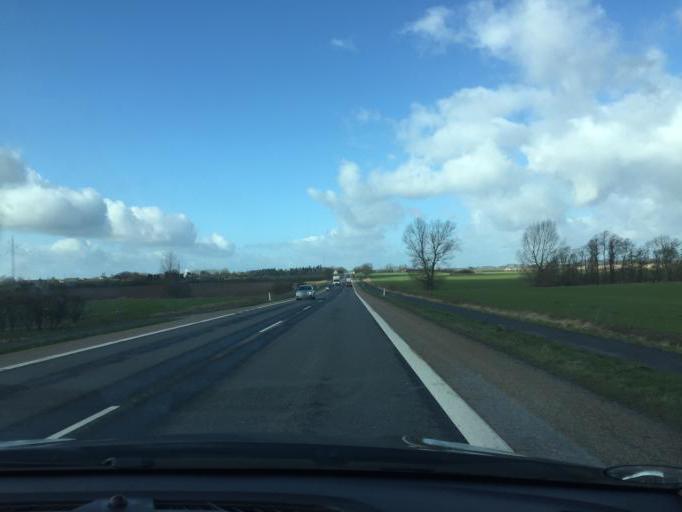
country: DK
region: South Denmark
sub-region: Middelfart Kommune
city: Norre Aby
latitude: 55.4836
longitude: 9.8298
